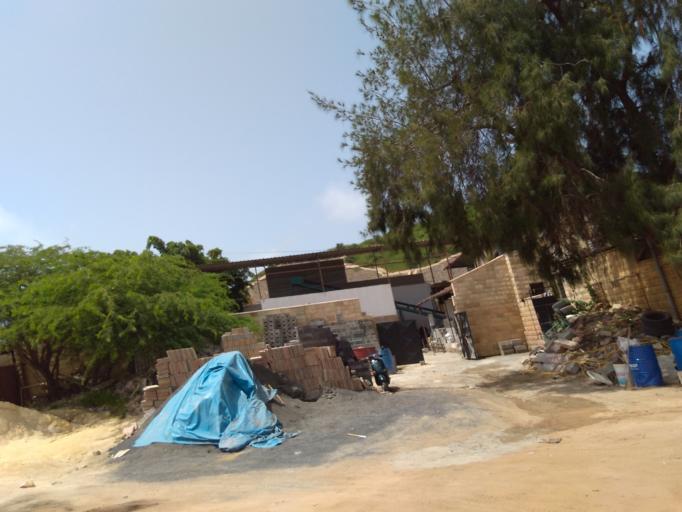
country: SN
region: Dakar
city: Mermoz Boabab
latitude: 14.7230
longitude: -17.4932
